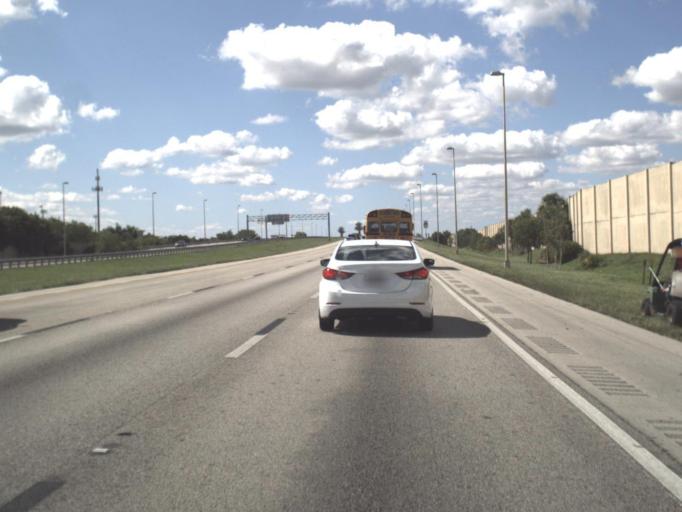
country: US
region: Florida
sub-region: Broward County
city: Parkland
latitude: 26.3022
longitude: -80.2613
